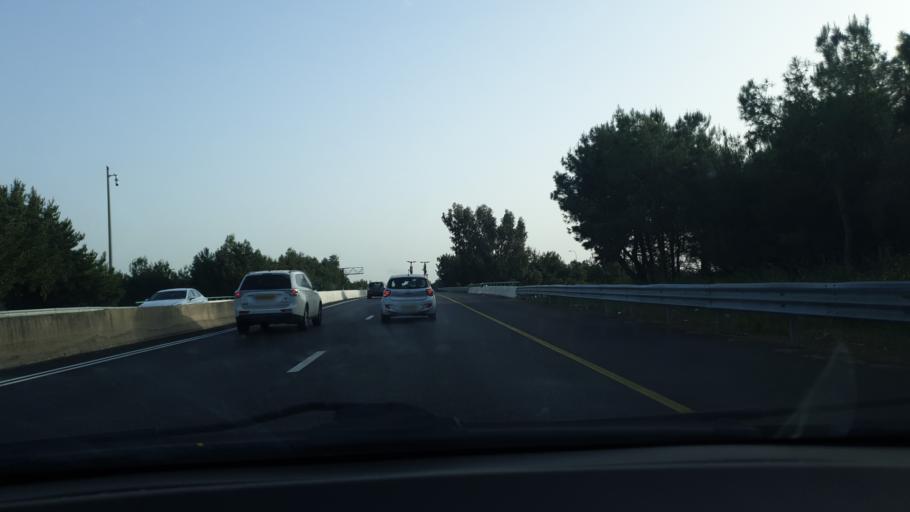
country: IL
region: Central District
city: Even Yehuda
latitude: 32.2358
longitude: 34.8855
